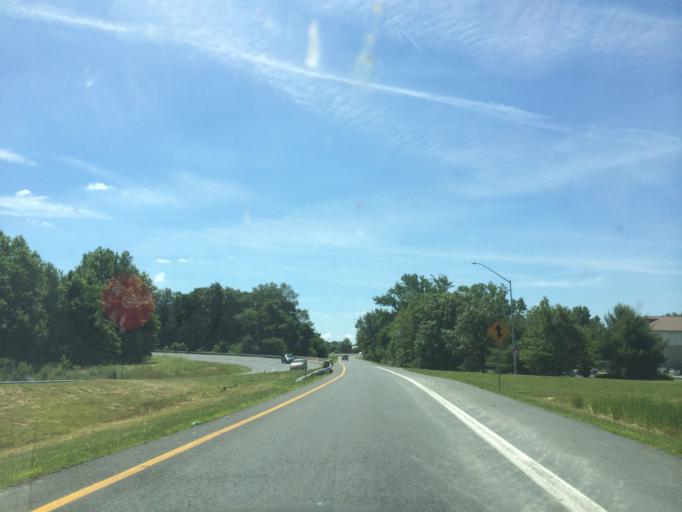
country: US
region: Maryland
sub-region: Wicomico County
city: Salisbury
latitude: 38.3683
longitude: -75.5397
